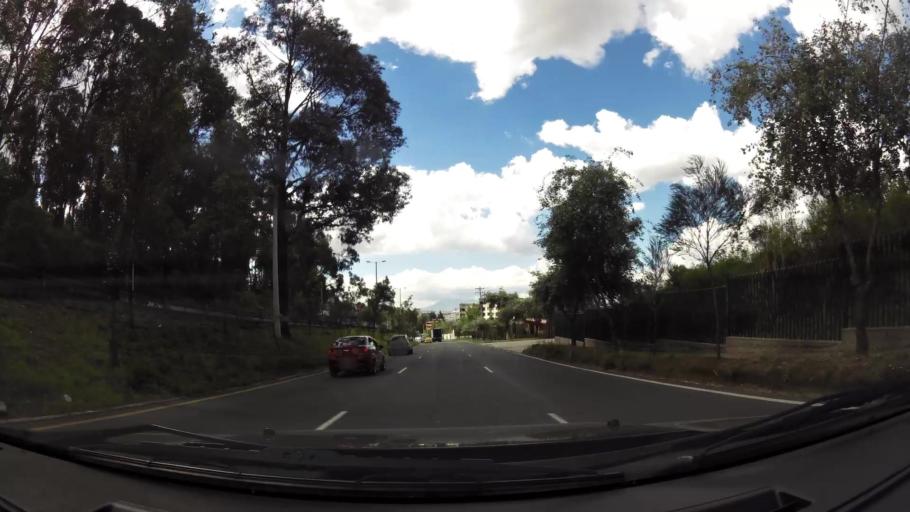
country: EC
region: Pichincha
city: Quito
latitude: -0.1771
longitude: -78.5023
